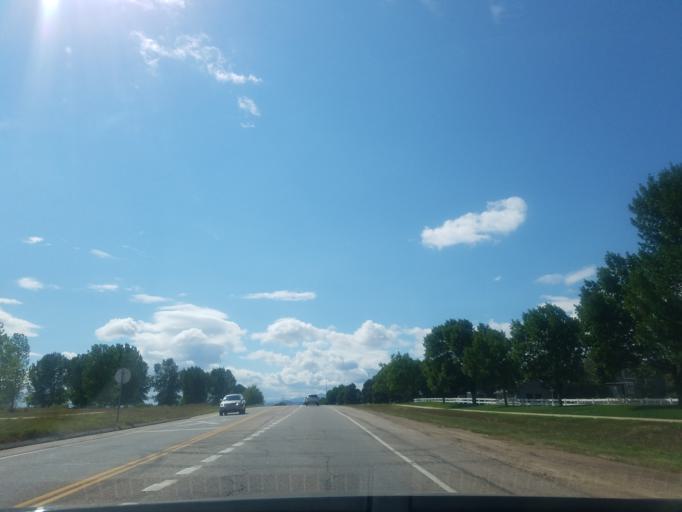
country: US
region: Colorado
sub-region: Larimer County
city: Loveland
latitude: 40.4802
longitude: -105.0430
